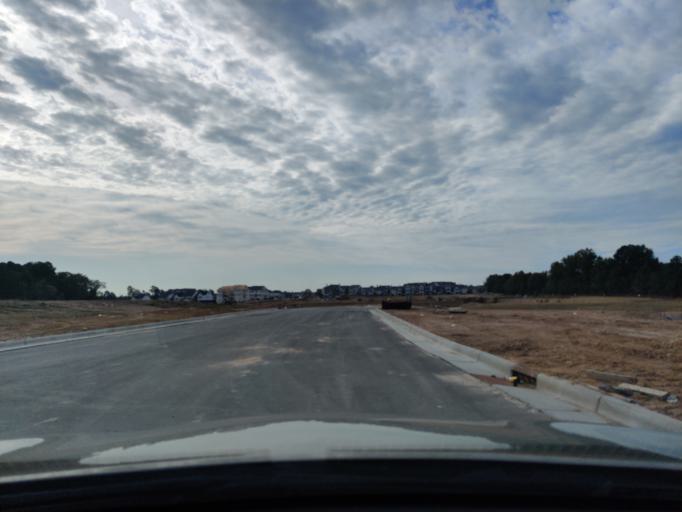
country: US
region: North Carolina
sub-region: Wake County
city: Morrisville
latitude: 35.8277
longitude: -78.8577
